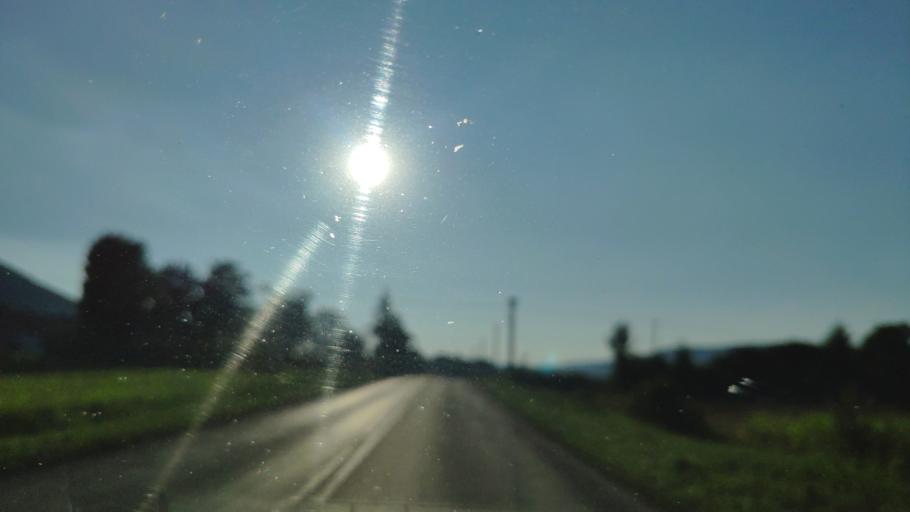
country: SK
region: Presovsky
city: Chlmec
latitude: 48.9303
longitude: 21.9725
